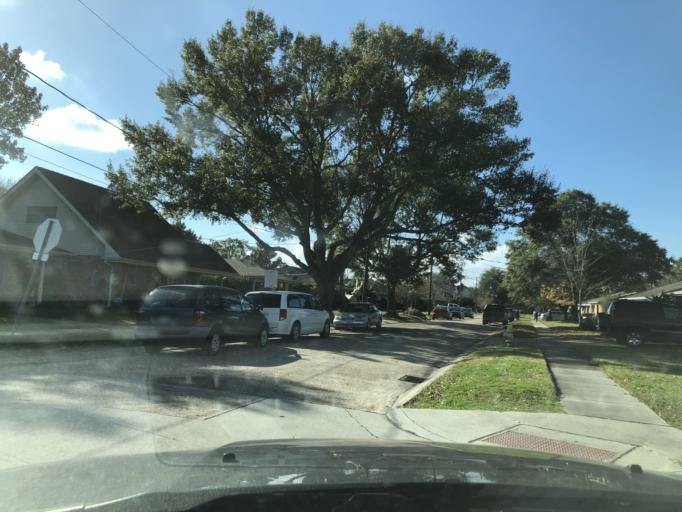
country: US
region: Louisiana
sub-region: Jefferson Parish
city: Metairie Terrace
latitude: 29.9863
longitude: -90.1643
